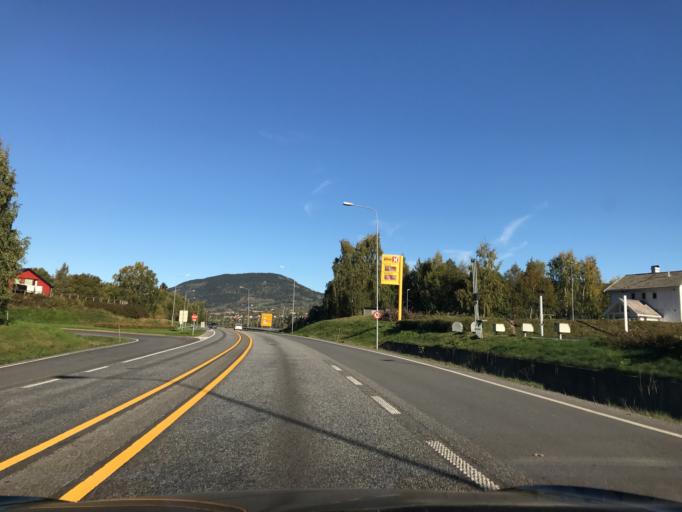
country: NO
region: Oppland
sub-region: Lillehammer
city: Lillehammer
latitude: 61.1063
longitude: 10.4429
